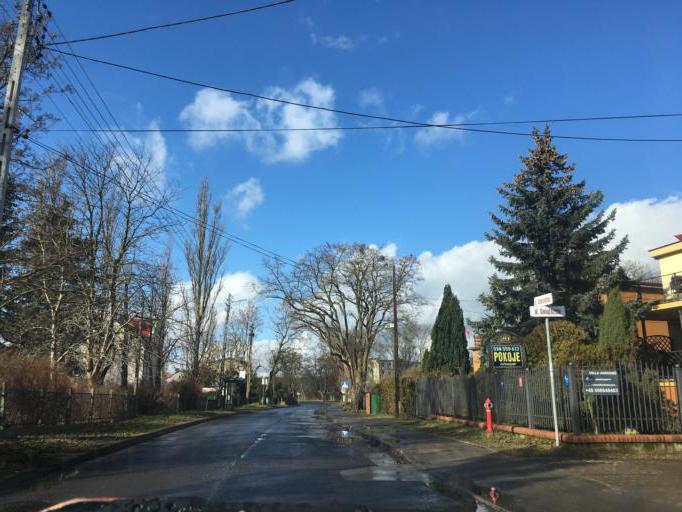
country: PL
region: Pomeranian Voivodeship
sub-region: Powiat gdanski
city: Cedry Wielkie
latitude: 54.3457
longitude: 18.8211
